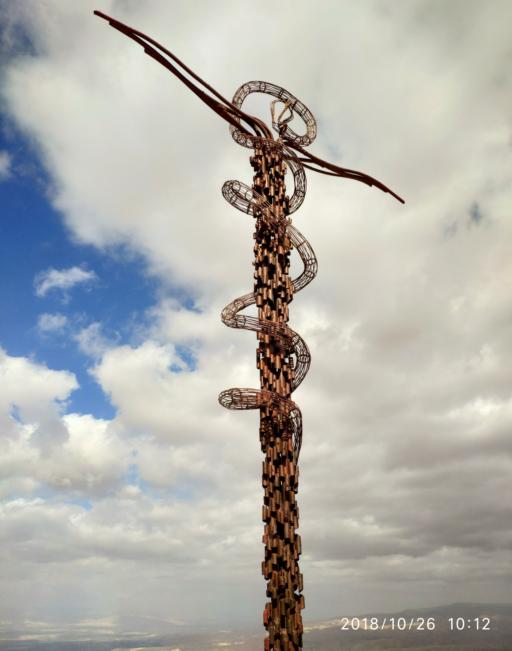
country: JO
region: Madaba
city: Madaba
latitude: 31.7683
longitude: 35.7254
